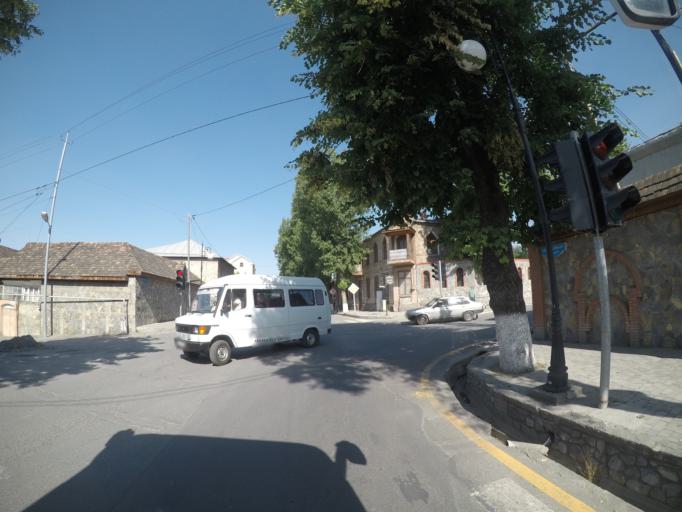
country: AZ
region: Shaki City
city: Sheki
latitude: 41.2059
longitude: 47.1745
